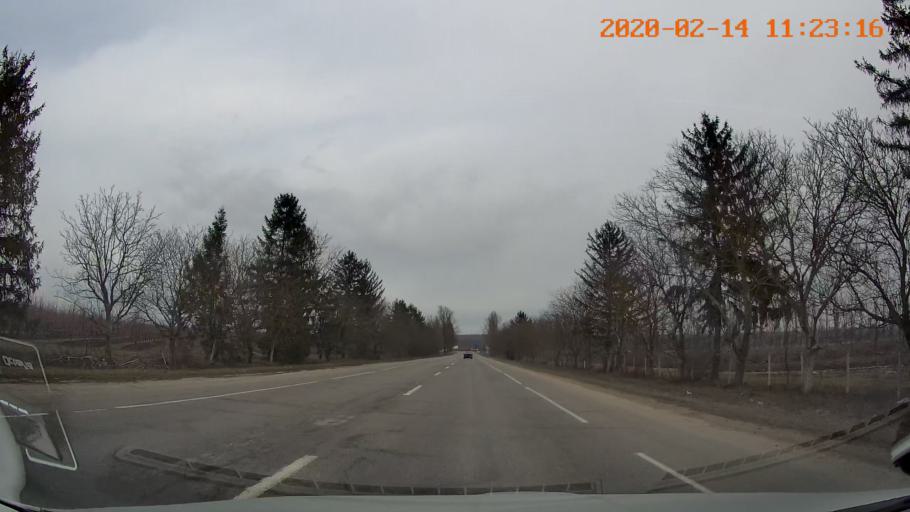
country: MD
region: Briceni
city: Briceni
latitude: 48.3219
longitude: 27.1228
